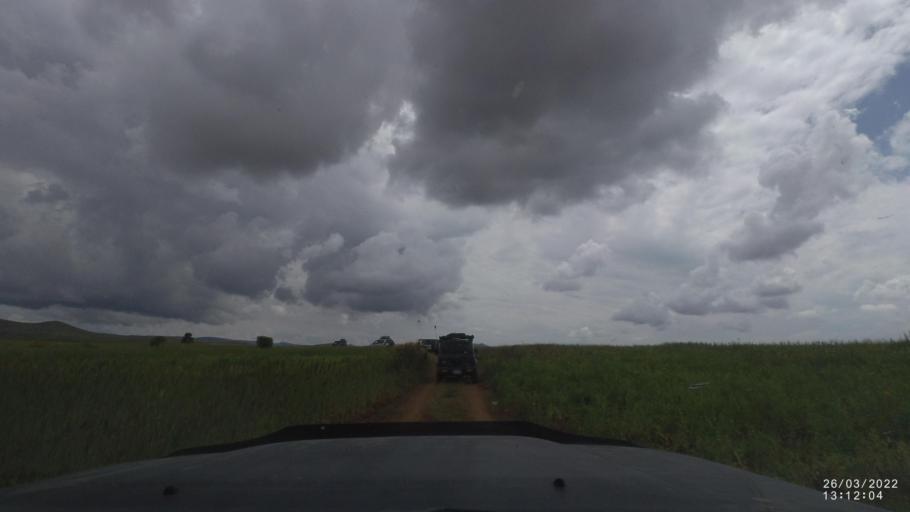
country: BO
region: Cochabamba
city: Cliza
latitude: -17.7366
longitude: -65.8604
